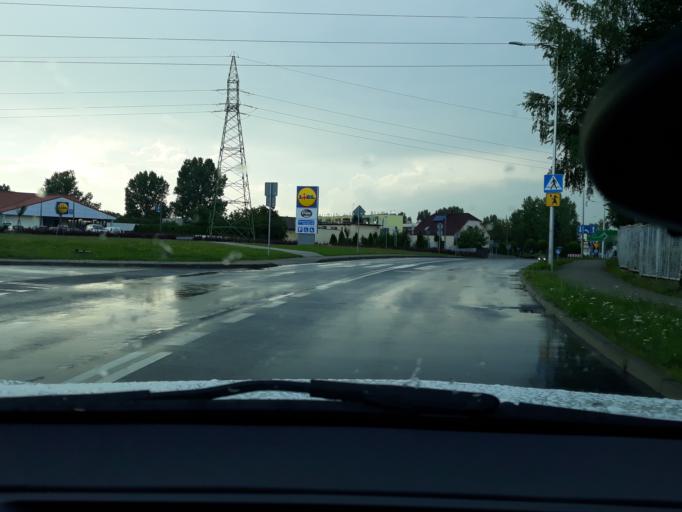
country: PL
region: Lesser Poland Voivodeship
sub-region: Powiat oswiecimski
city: Babice
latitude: 50.0776
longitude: 19.1649
